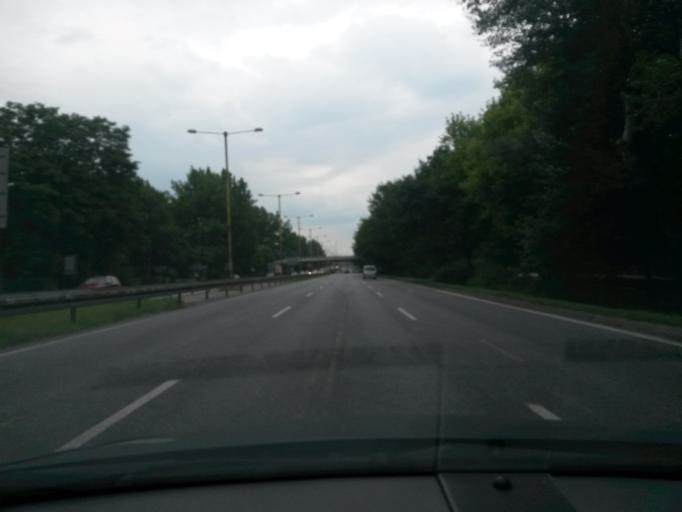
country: PL
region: Silesian Voivodeship
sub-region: Czestochowa
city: Czestochowa
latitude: 50.8148
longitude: 19.1375
